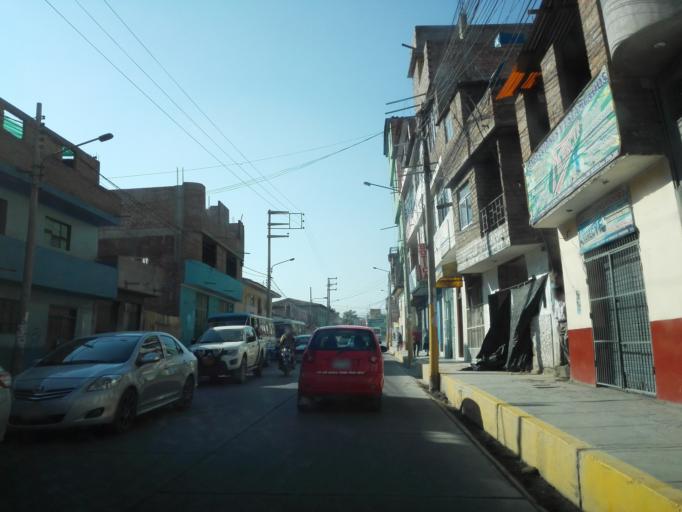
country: PE
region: Ayacucho
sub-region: Provincia de Huamanga
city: Ayacucho
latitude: -13.1651
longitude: -74.2166
